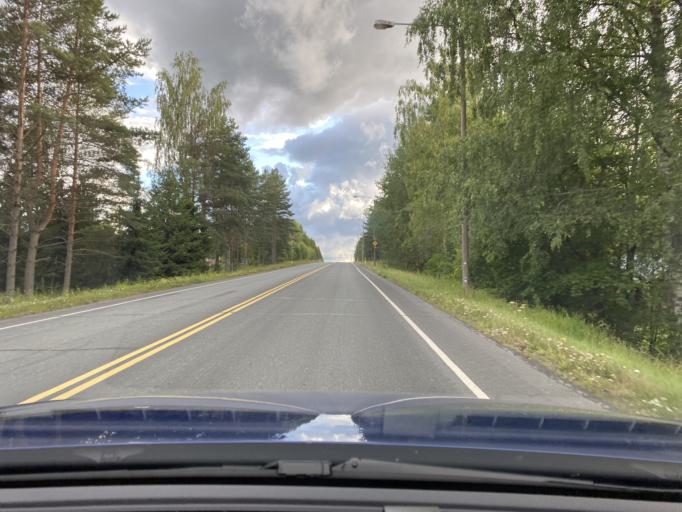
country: FI
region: Haeme
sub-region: Haemeenlinna
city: Renko
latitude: 60.8962
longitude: 24.2751
